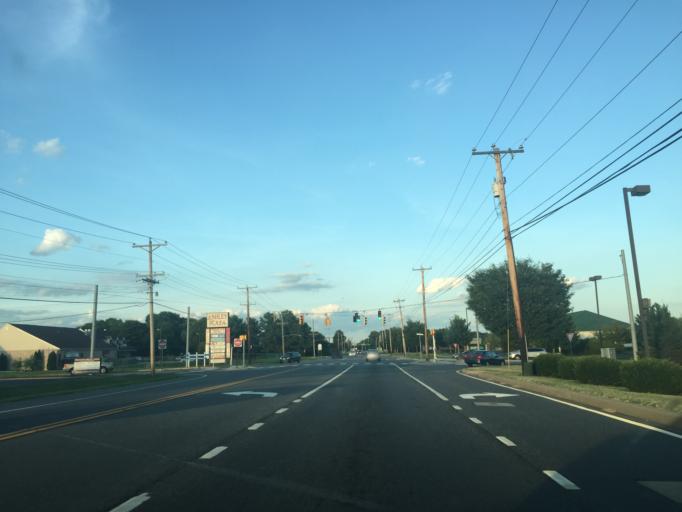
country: US
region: Delaware
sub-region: New Castle County
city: Middletown
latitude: 39.4504
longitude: -75.7027
